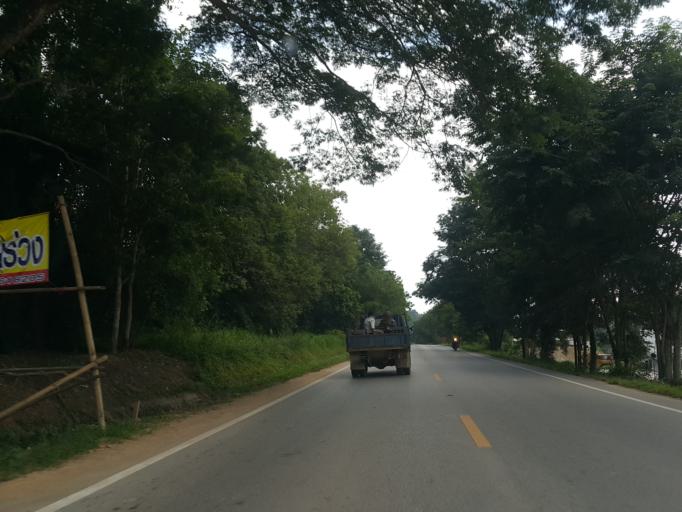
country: TH
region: Chiang Mai
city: Phrao
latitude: 19.2884
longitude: 99.1879
